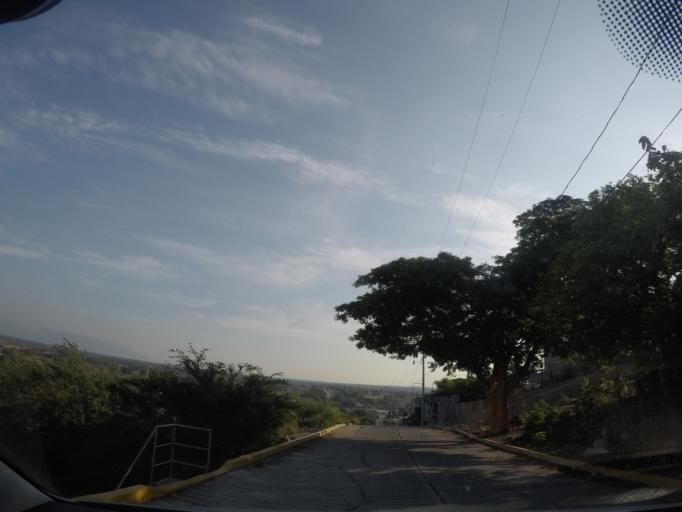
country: MX
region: Oaxaca
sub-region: Santo Domingo Tehuantepec
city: La Noria
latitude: 16.2432
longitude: -95.1504
